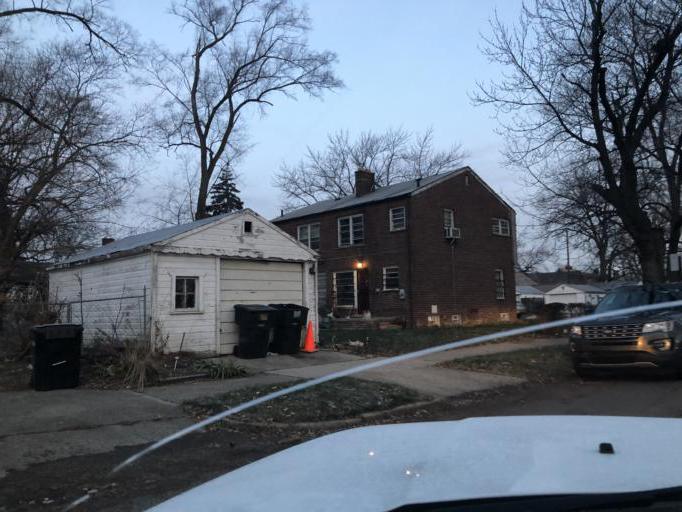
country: US
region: Michigan
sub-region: Oakland County
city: Oak Park
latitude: 42.4080
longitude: -83.2166
